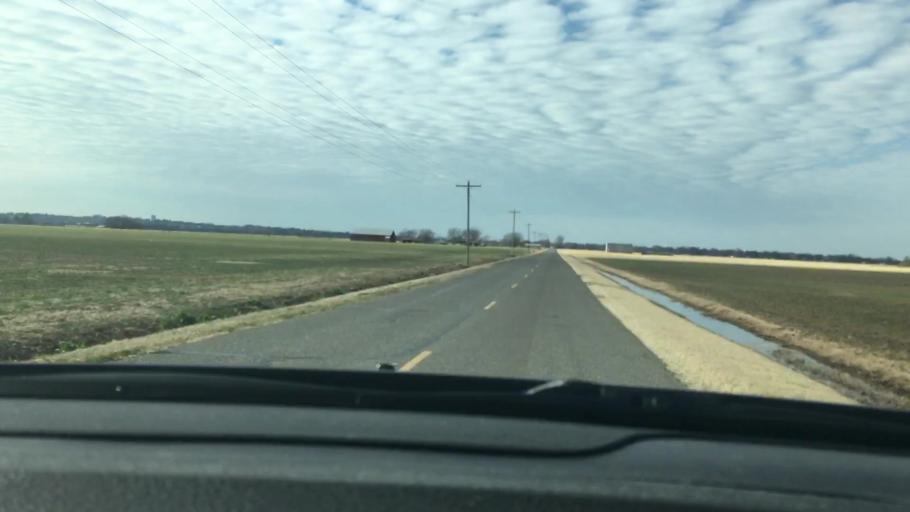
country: US
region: Oklahoma
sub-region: Garvin County
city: Pauls Valley
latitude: 34.7387
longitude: -97.1802
